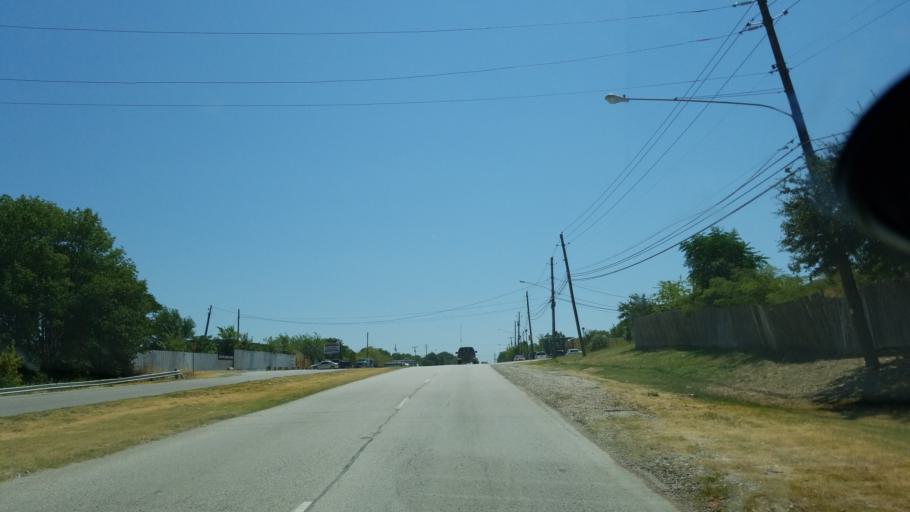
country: US
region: Texas
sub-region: Dallas County
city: Cockrell Hill
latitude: 32.7474
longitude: -96.9161
